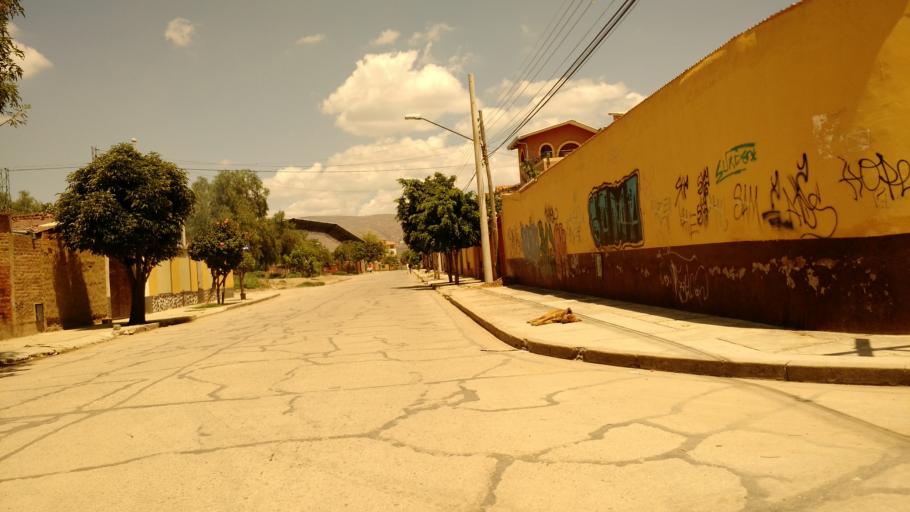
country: BO
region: Cochabamba
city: Cochabamba
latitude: -17.4340
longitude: -66.1536
